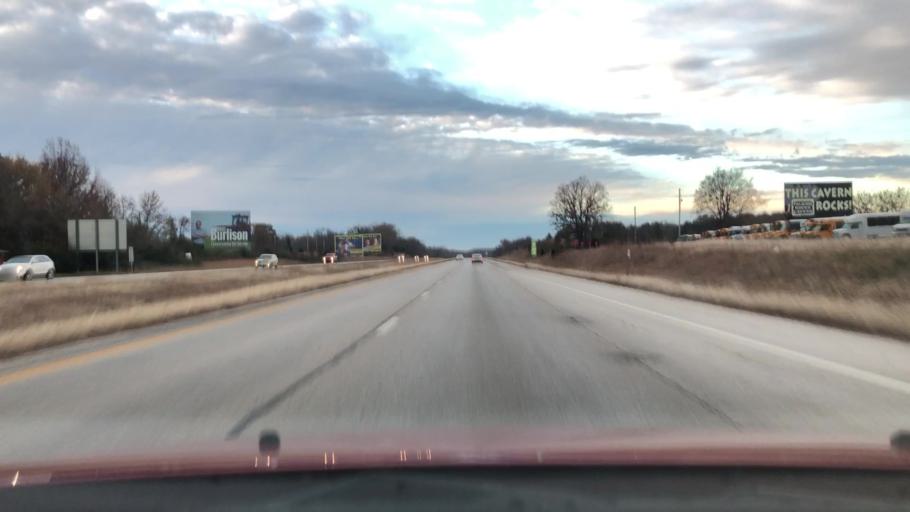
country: US
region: Missouri
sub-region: Christian County
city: Ozark
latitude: 36.9387
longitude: -93.2323
